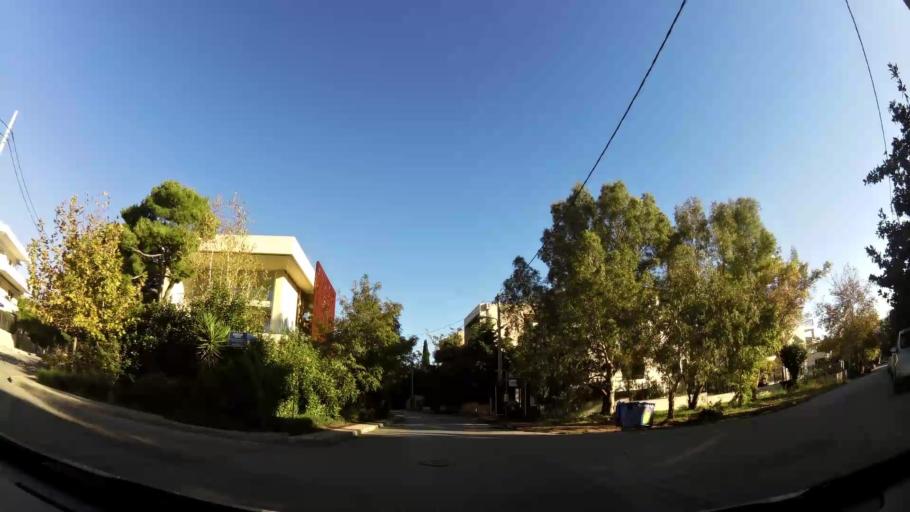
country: GR
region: Attica
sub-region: Nomarchia Athinas
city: Kifisia
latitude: 38.0849
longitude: 23.8028
